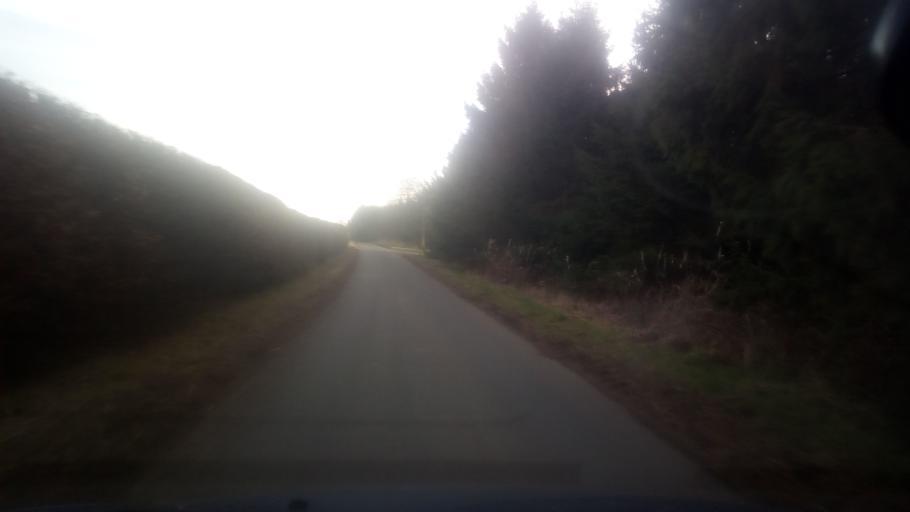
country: GB
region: Scotland
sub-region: The Scottish Borders
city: Jedburgh
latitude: 55.4179
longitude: -2.6191
